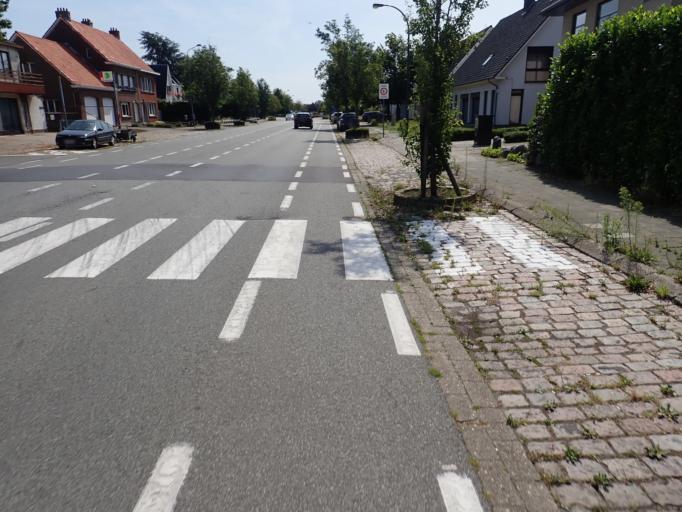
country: BE
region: Flanders
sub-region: Provincie Antwerpen
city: Wommelgem
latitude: 51.2082
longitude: 4.5047
